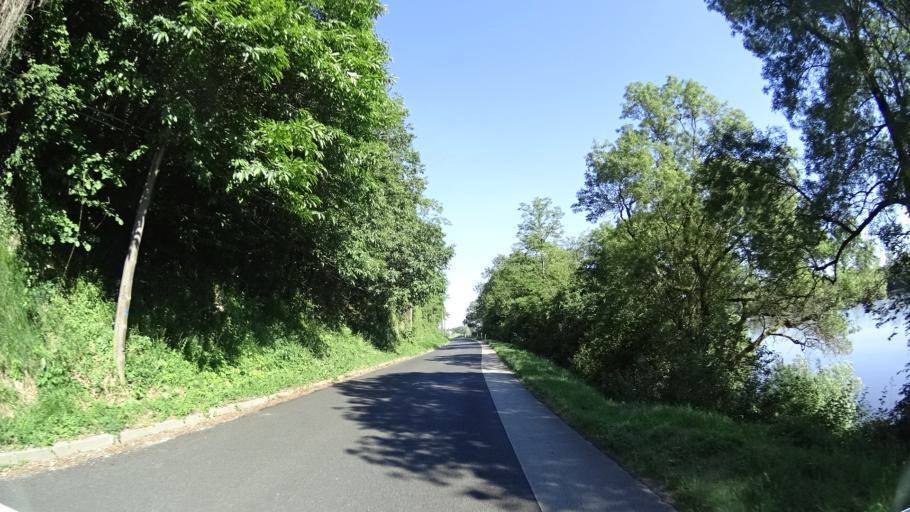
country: FR
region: Pays de la Loire
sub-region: Departement de Maine-et-Loire
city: Saint-Martin-de-la-Place
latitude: 47.3033
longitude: -0.1454
